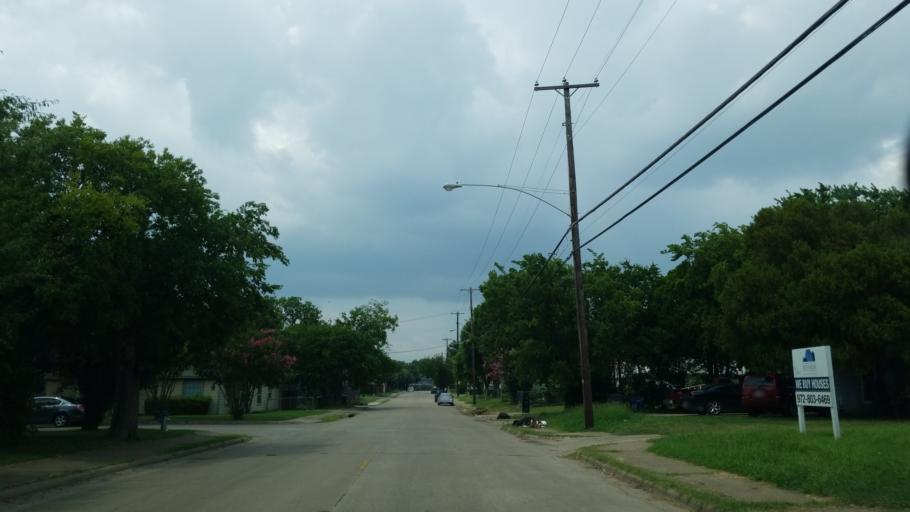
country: US
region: Texas
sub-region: Dallas County
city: University Park
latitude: 32.8483
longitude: -96.8301
